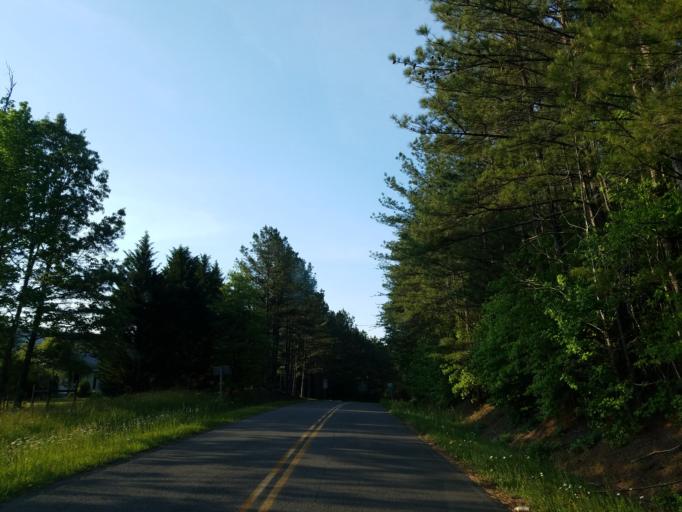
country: US
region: Georgia
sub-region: Gordon County
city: Calhoun
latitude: 34.5863
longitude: -85.0863
